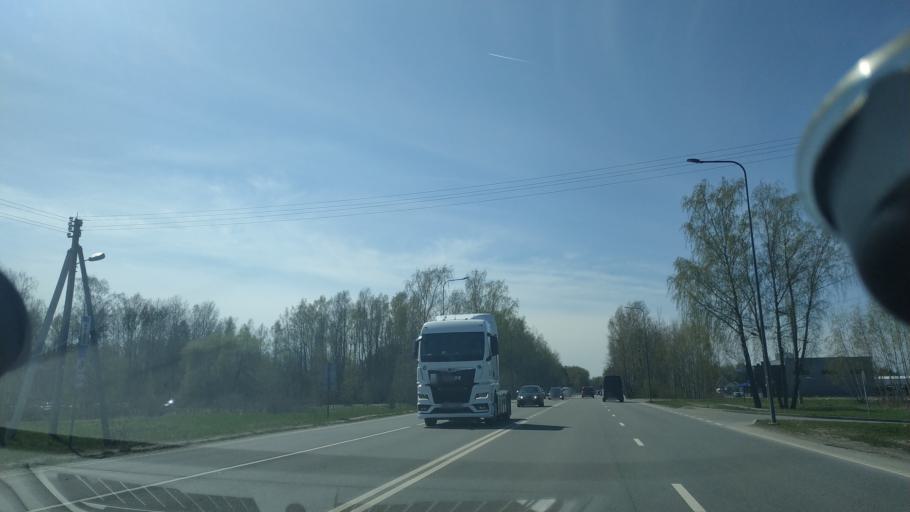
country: LT
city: Ramuciai
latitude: 54.9218
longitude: 24.0467
